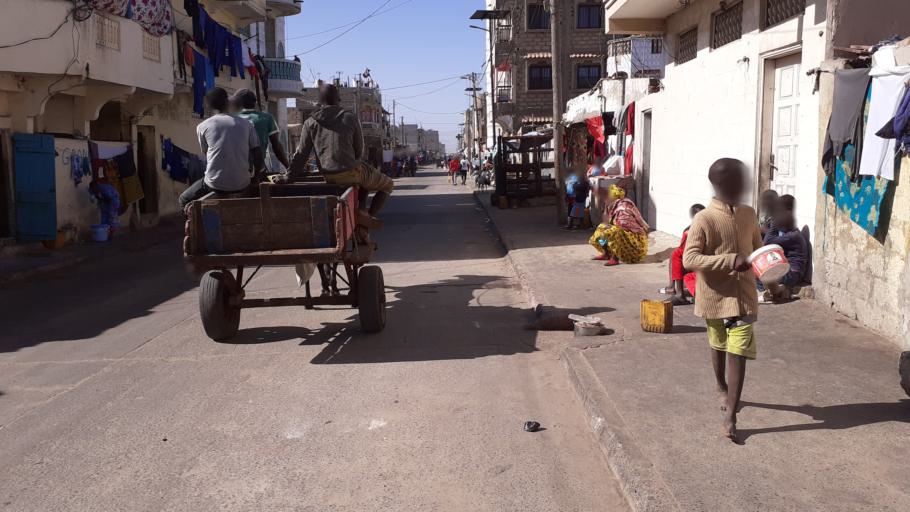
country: SN
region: Saint-Louis
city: Saint-Louis
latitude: 16.0234
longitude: -16.5087
